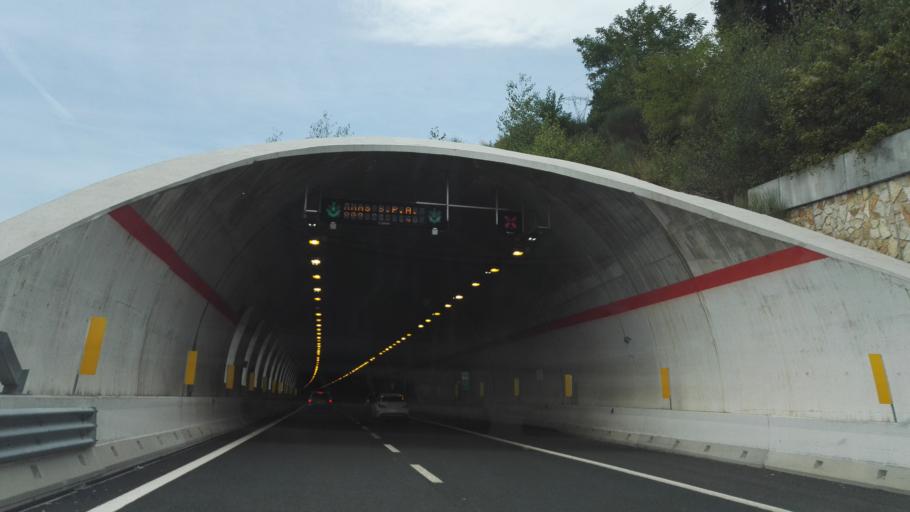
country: IT
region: Basilicate
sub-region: Provincia di Potenza
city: Nemoli
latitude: 40.0969
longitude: 15.8108
